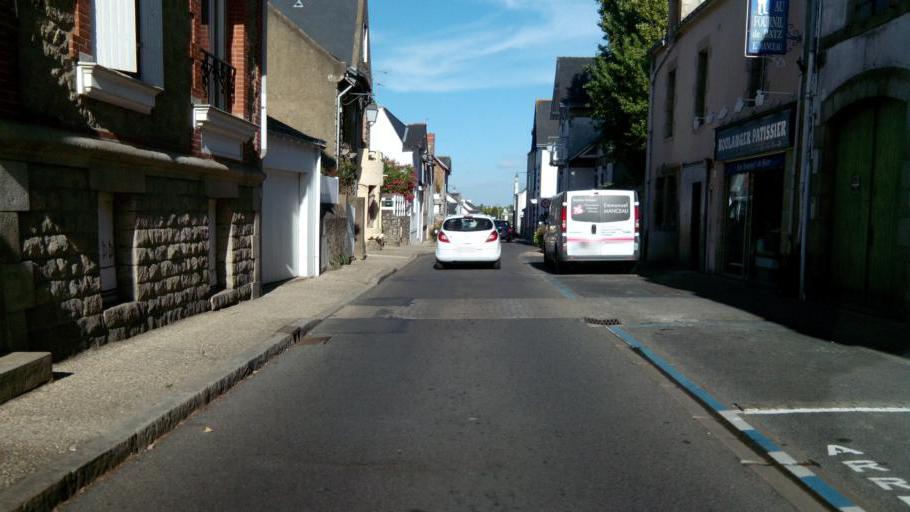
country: FR
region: Pays de la Loire
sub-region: Departement de la Loire-Atlantique
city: Batz-sur-Mer
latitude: 47.2777
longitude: -2.4769
